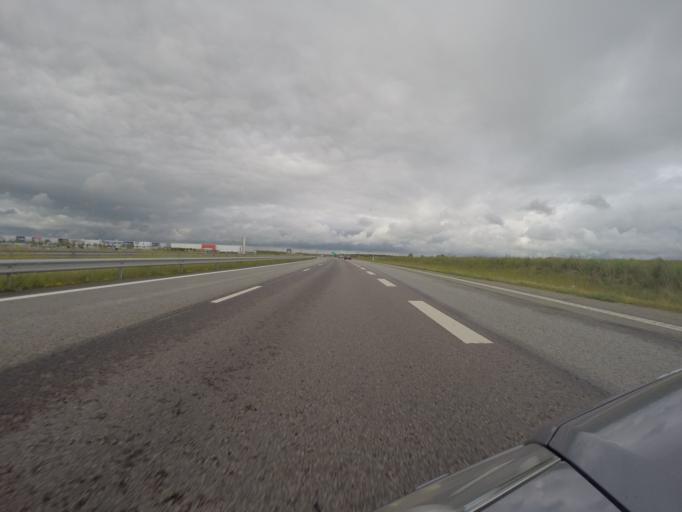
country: SE
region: Skane
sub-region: Burlovs Kommun
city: Arloev
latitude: 55.6099
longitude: 13.1016
